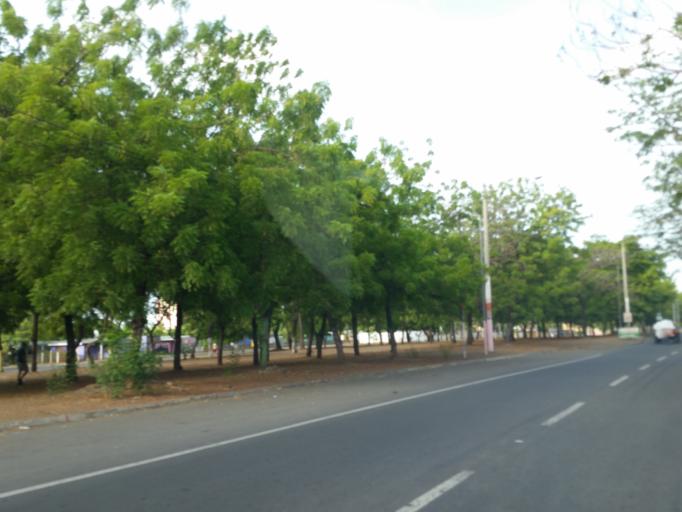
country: NI
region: Managua
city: Managua
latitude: 12.1546
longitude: -86.2783
